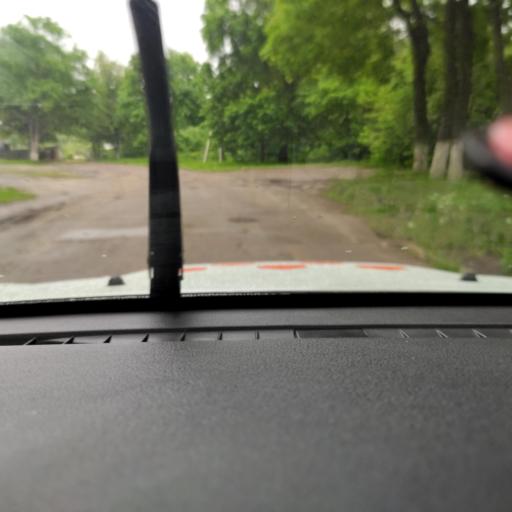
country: RU
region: Voronezj
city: Devitsa
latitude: 51.6052
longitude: 39.0005
